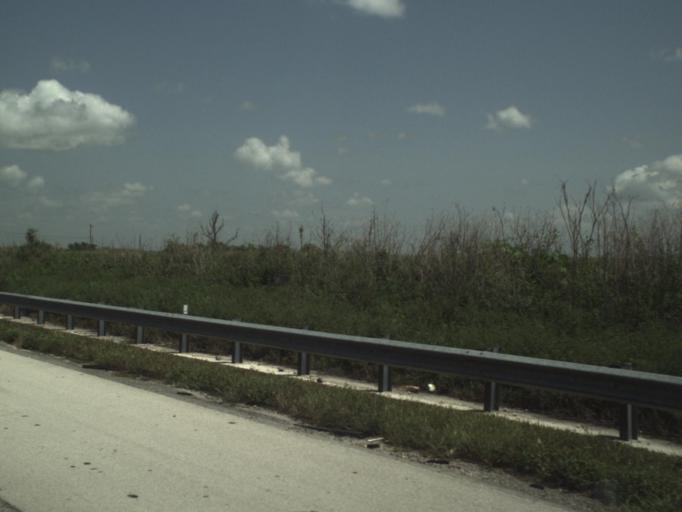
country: US
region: Florida
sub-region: Palm Beach County
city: Belle Glade Camp
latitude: 26.3831
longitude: -80.5749
